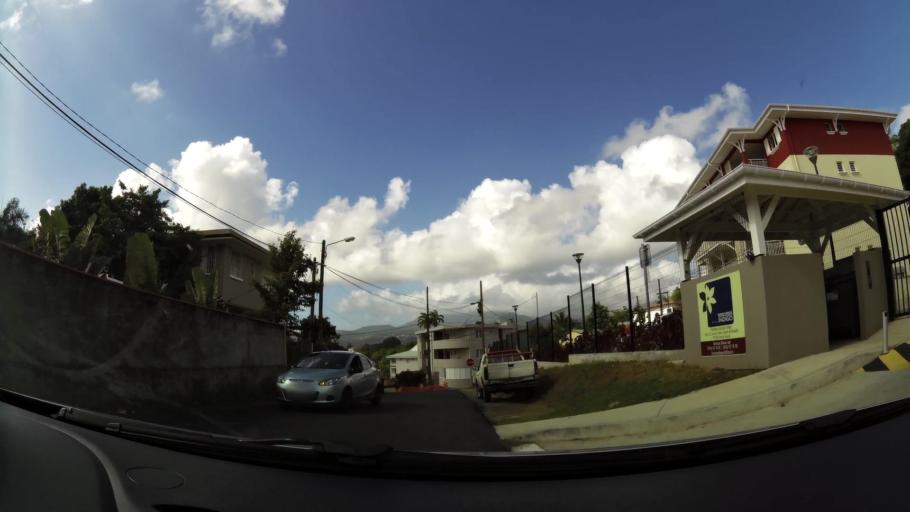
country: MQ
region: Martinique
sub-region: Martinique
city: Fort-de-France
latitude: 14.6266
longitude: -61.0591
